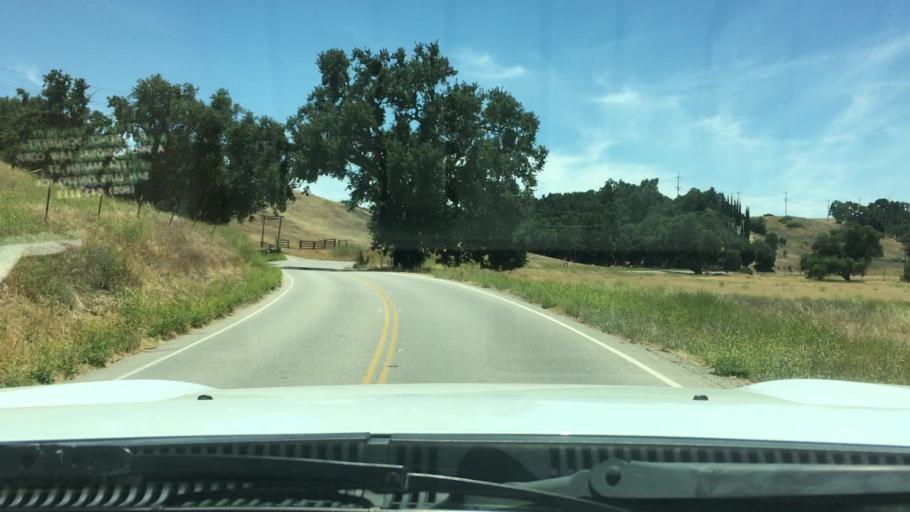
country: US
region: California
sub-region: San Luis Obispo County
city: Templeton
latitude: 35.5532
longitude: -120.6918
